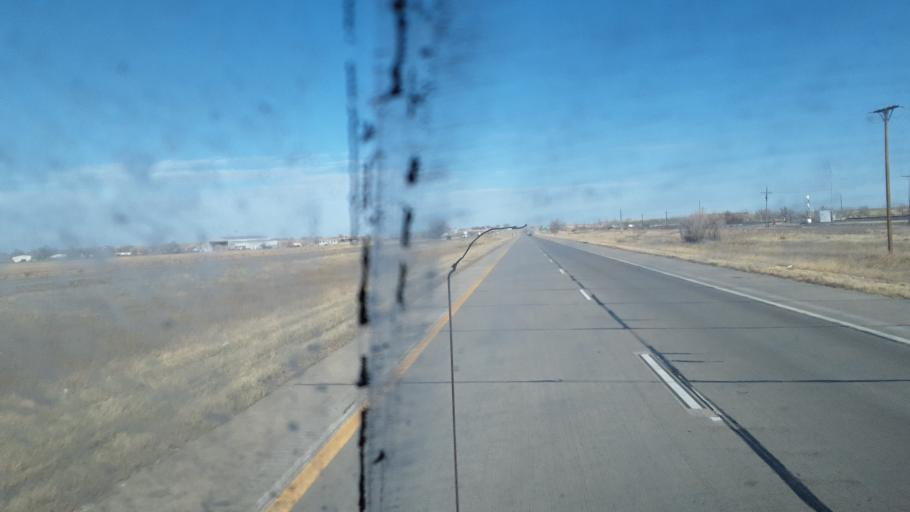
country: US
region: Colorado
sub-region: Weld County
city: Hudson
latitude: 40.0940
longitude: -104.6139
